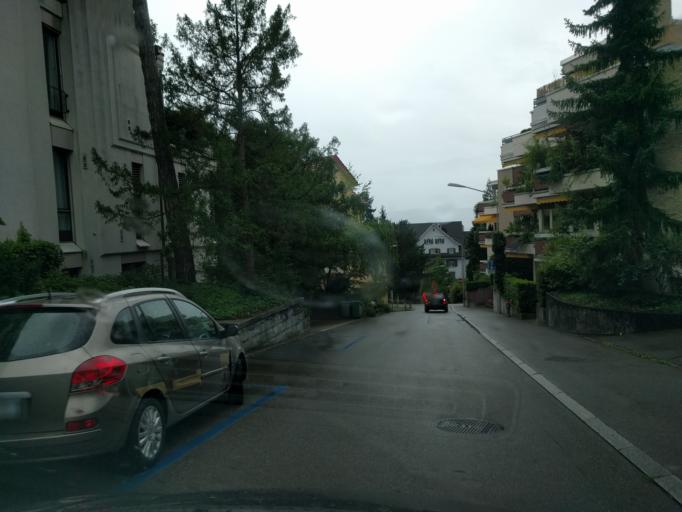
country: CH
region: Zurich
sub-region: Bezirk Zuerich
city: Zuerich (Kreis 7) / Hottingen
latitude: 47.3715
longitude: 8.5641
